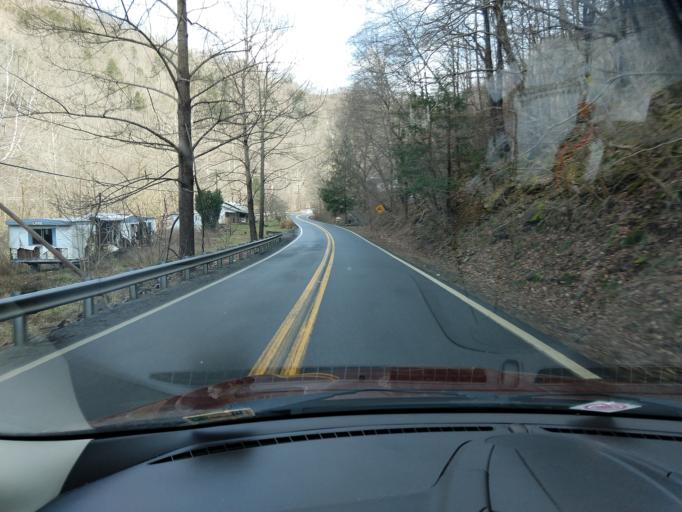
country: US
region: West Virginia
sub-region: McDowell County
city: Welch
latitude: 37.3431
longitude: -81.7532
